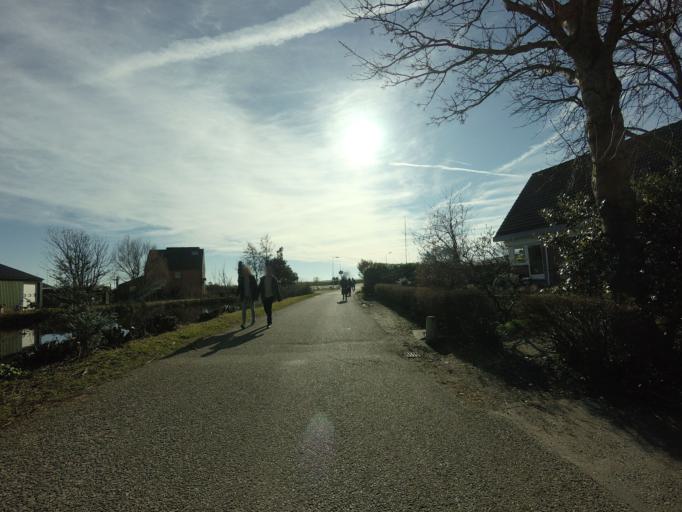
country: NL
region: South Holland
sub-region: Gemeente Kaag en Braassem
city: Oude Wetering
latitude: 52.1965
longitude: 4.6388
